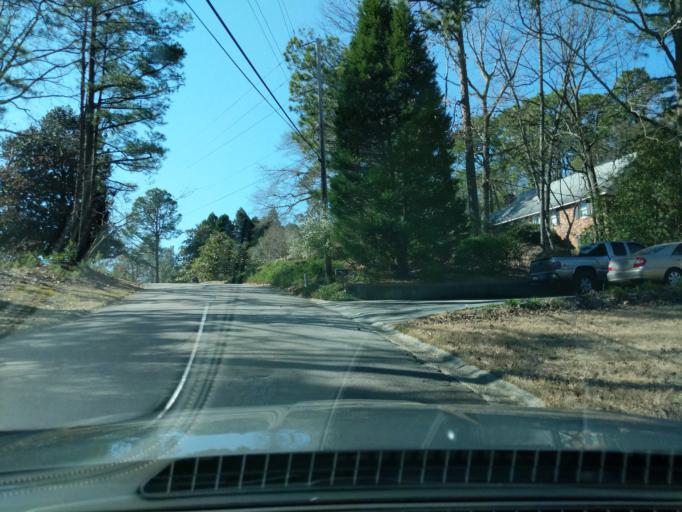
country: US
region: South Carolina
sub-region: Aiken County
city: Aiken
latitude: 33.5309
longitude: -81.7351
